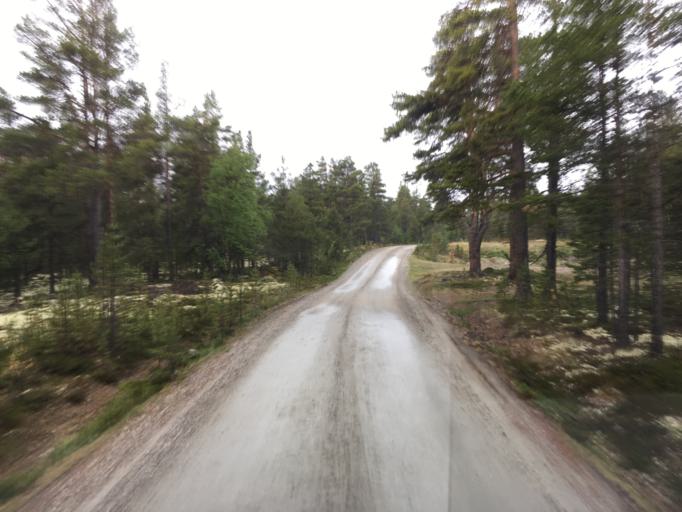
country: NO
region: Hedmark
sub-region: Folldal
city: Folldal
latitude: 62.0672
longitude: 9.9347
